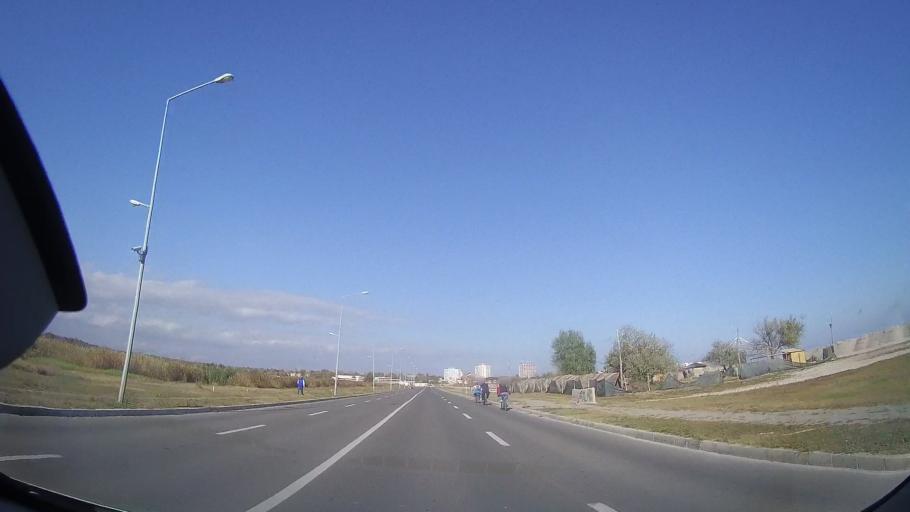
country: RO
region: Constanta
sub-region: Municipiul Mangalia
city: Mangalia
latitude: 43.8364
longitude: 28.5892
